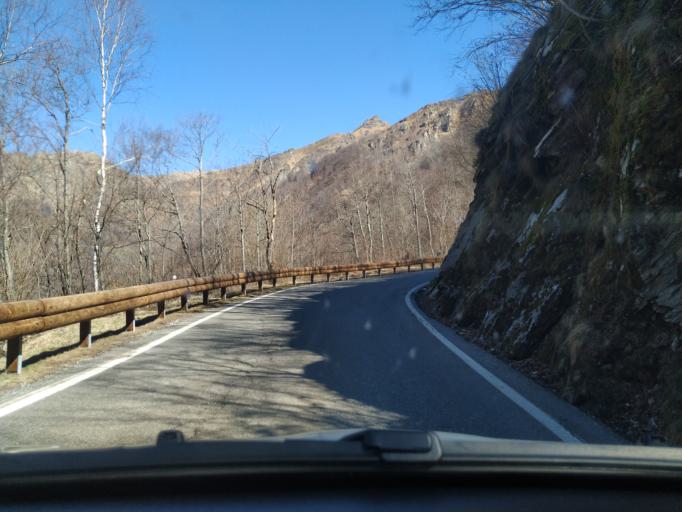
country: IT
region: Piedmont
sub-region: Provincia di Vercelli
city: Rimella
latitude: 45.9091
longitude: 8.1789
